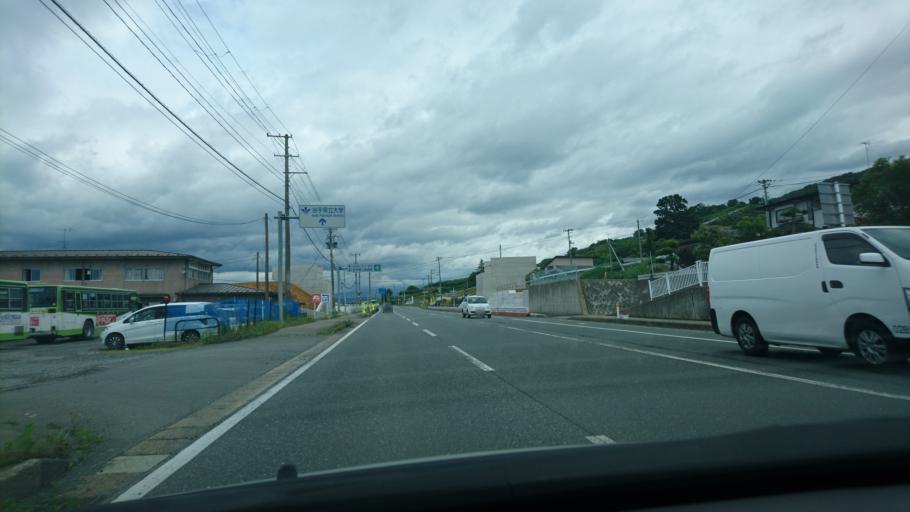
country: JP
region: Iwate
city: Morioka-shi
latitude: 39.6591
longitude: 141.1798
